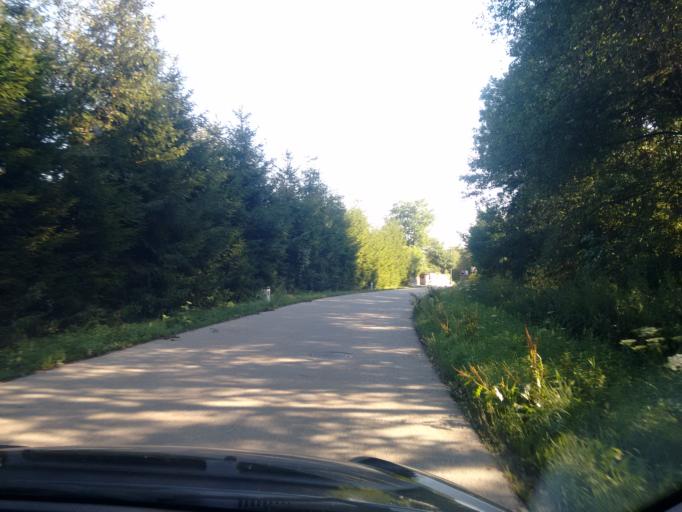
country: AT
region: Upper Austria
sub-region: Wels-Land
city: Buchkirchen
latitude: 48.2350
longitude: 13.9720
